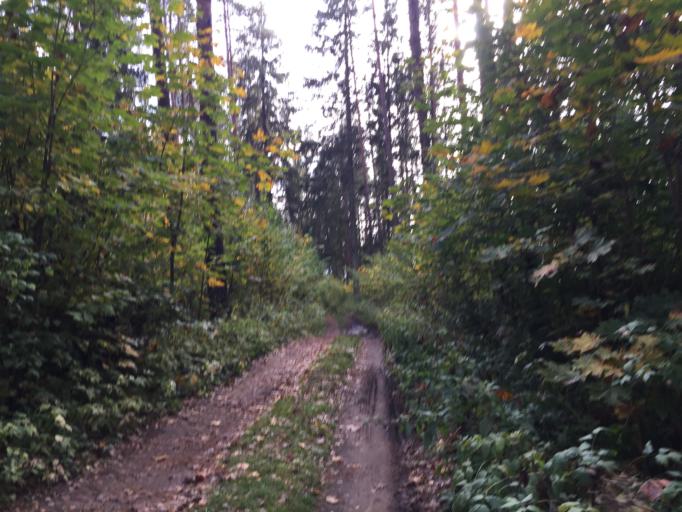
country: LV
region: Jaunpils
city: Jaunpils
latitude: 56.5979
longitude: 23.0146
